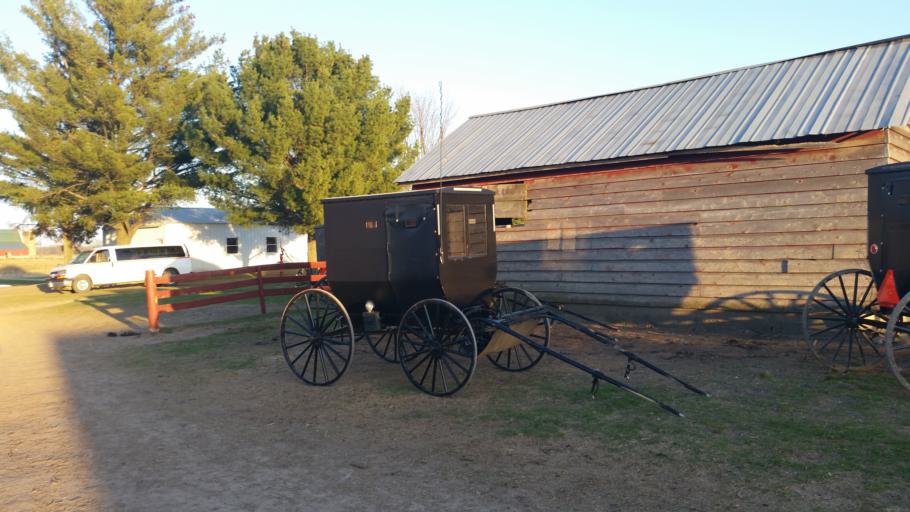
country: US
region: Wisconsin
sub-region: Clark County
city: Neillsville
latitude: 44.5565
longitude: -90.3999
